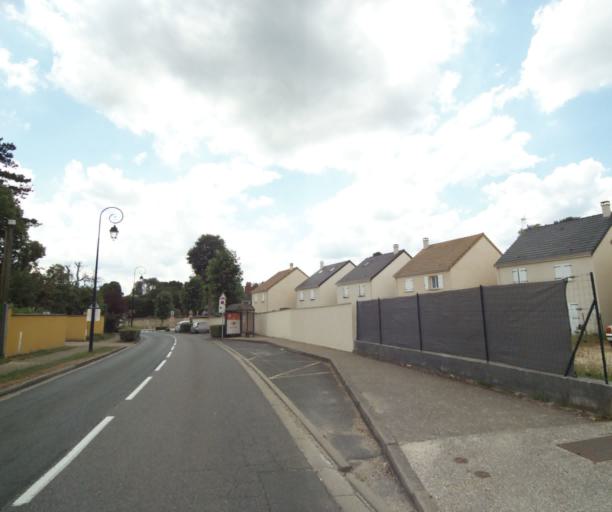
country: FR
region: Ile-de-France
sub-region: Departement de Seine-et-Marne
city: Vulaines-sur-Seine
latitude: 48.4318
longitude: 2.7668
